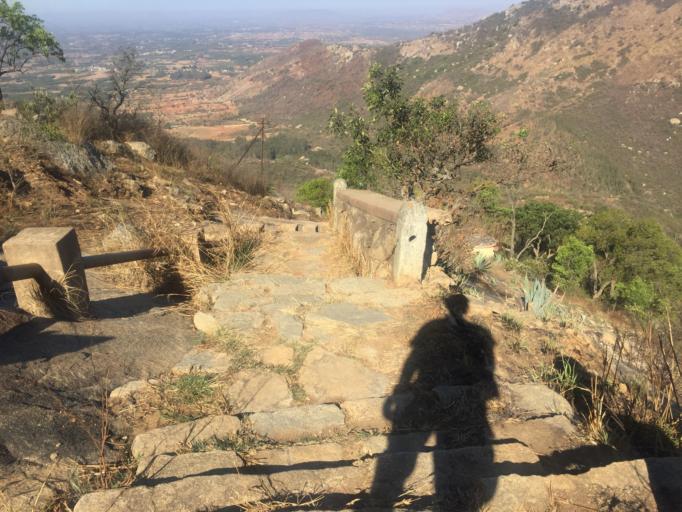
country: IN
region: Karnataka
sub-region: Chikkaballapur
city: Chik Ballapur
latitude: 13.3730
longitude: 77.6781
